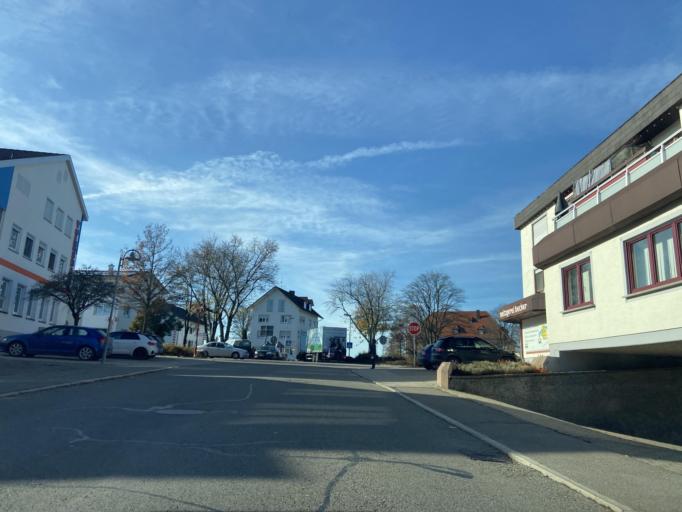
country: DE
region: Baden-Wuerttemberg
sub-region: Tuebingen Region
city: Stetten am Kalten Markt
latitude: 48.1221
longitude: 9.0783
